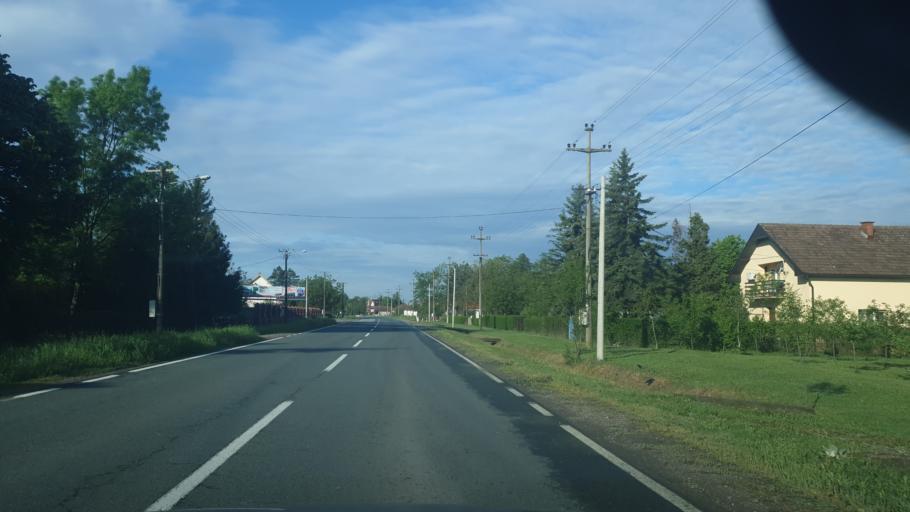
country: RS
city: Zvecka
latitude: 44.6134
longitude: 20.1612
